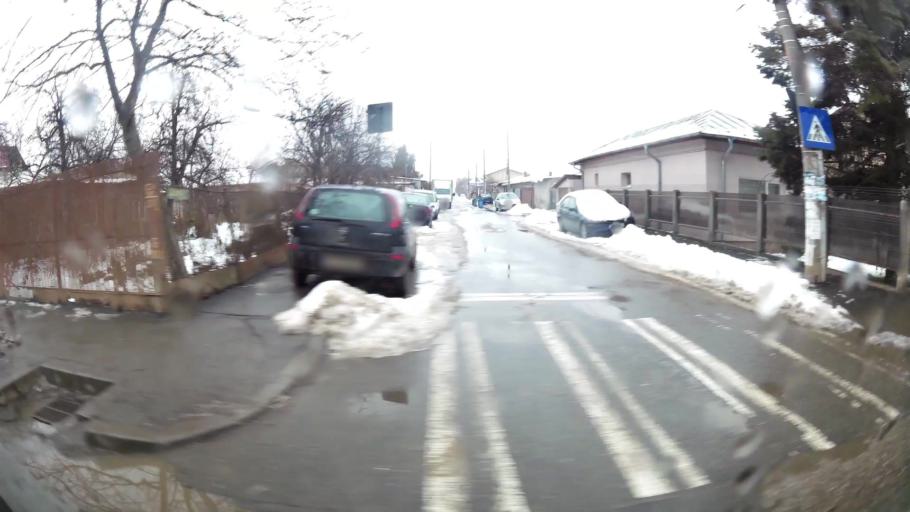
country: RO
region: Ilfov
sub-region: Comuna Chiajna
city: Rosu
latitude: 44.4069
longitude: 26.0170
